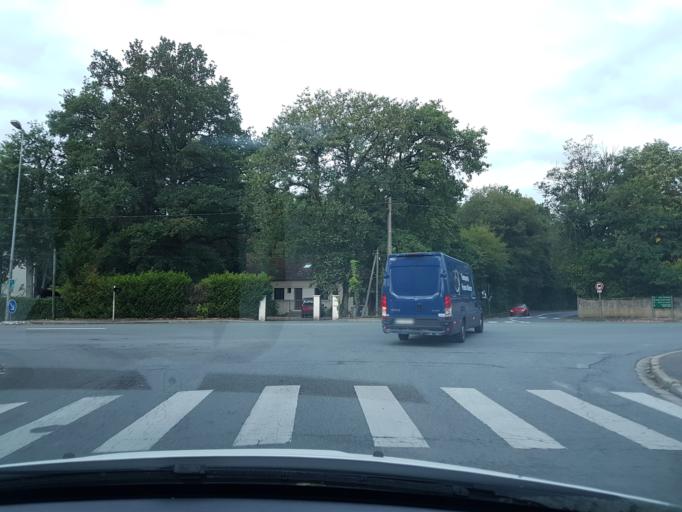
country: FR
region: Centre
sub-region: Departement d'Indre-et-Loire
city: Chambray-les-Tours
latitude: 47.3412
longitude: 0.7232
